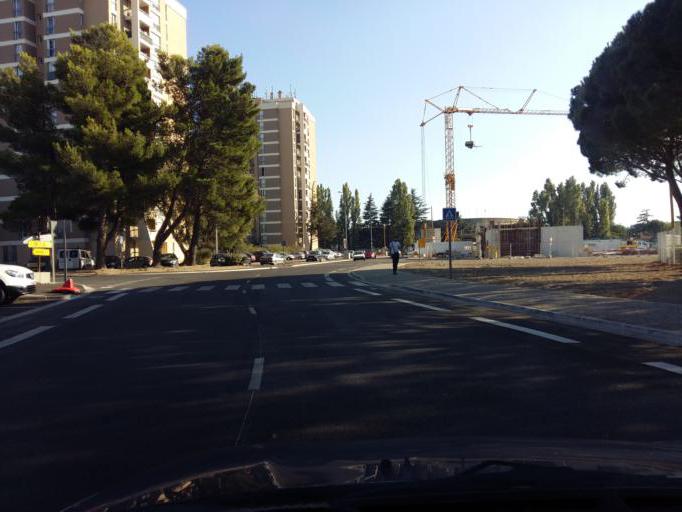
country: FR
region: Provence-Alpes-Cote d'Azur
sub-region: Departement du Vaucluse
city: Montfavet
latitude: 43.9322
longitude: 4.8407
